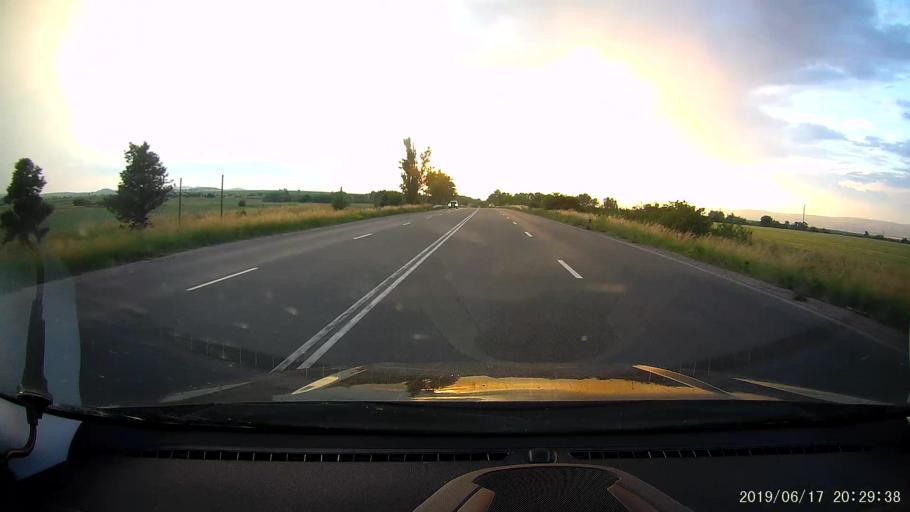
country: BG
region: Sofiya
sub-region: Obshtina Bozhurishte
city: Bozhurishte
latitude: 42.7881
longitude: 23.1582
